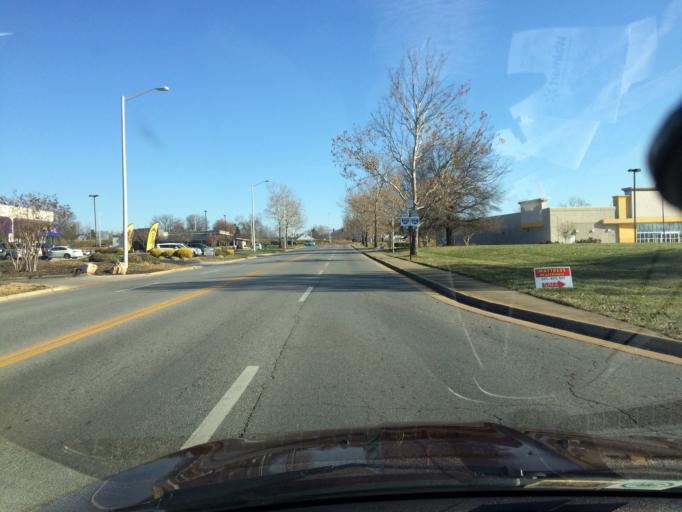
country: US
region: Virginia
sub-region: Roanoke County
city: Hollins
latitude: 37.3072
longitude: -79.9643
